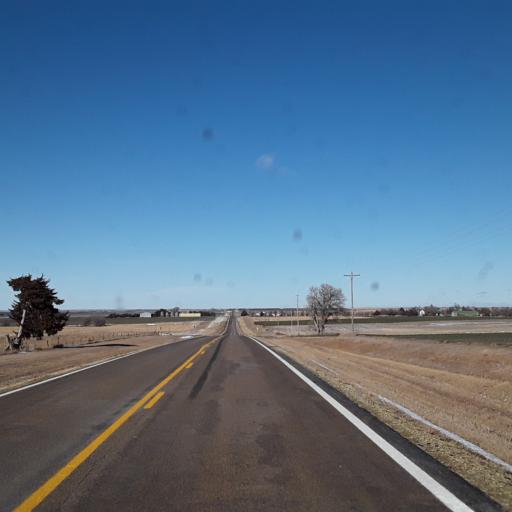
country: US
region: Kansas
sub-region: Mitchell County
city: Beloit
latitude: 39.3479
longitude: -98.1161
